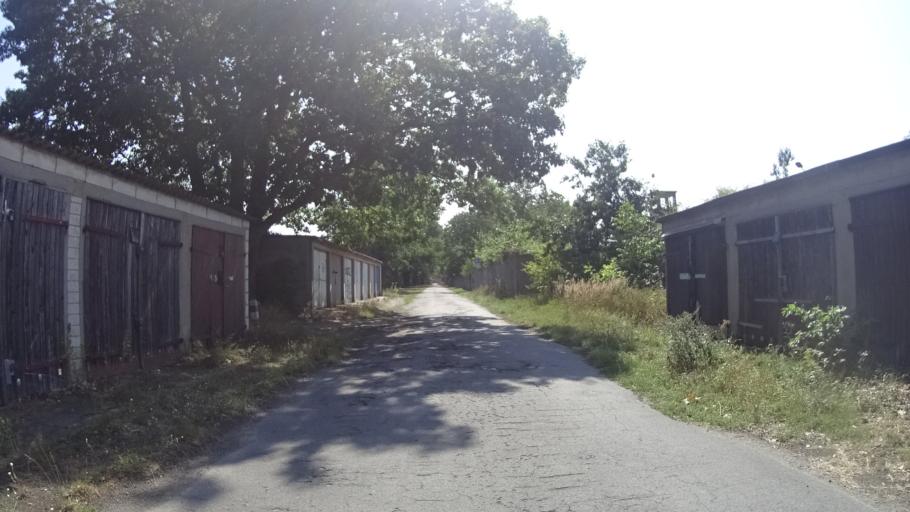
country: DE
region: Brandenburg
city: Cottbus
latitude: 51.7694
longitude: 14.3142
